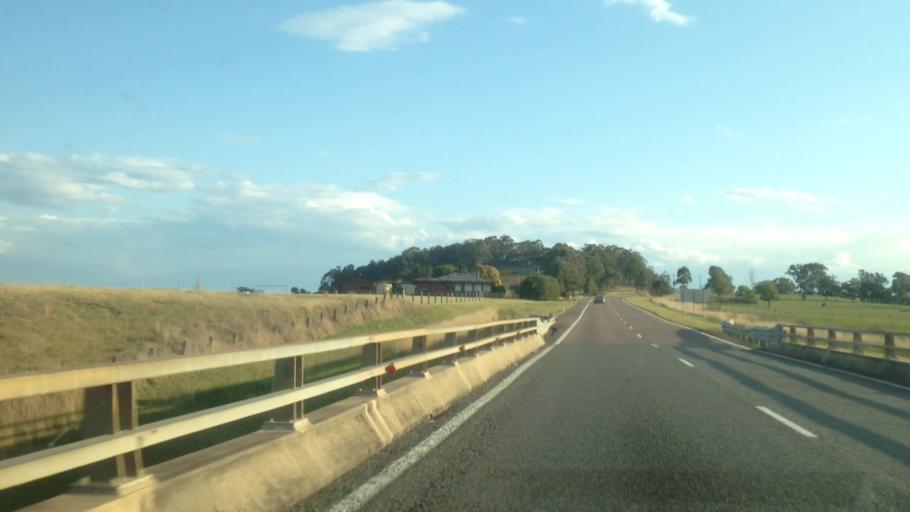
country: AU
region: New South Wales
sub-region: Cessnock
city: Kurri Kurri
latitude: -32.8784
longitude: 151.4742
